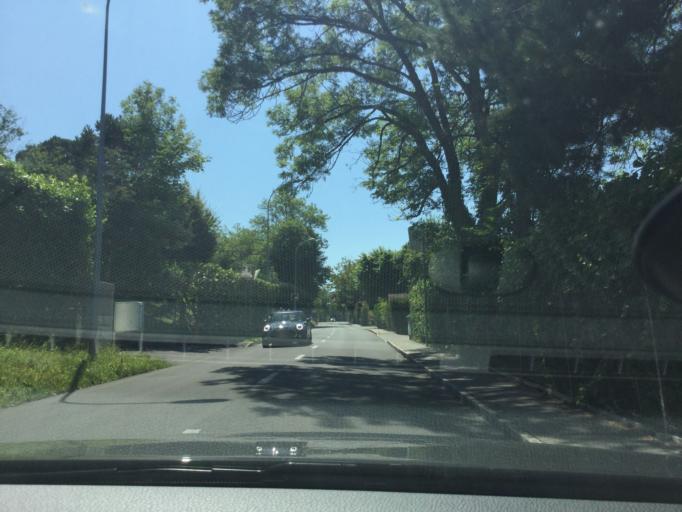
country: CH
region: Geneva
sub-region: Geneva
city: Anieres
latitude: 46.2787
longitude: 6.2250
